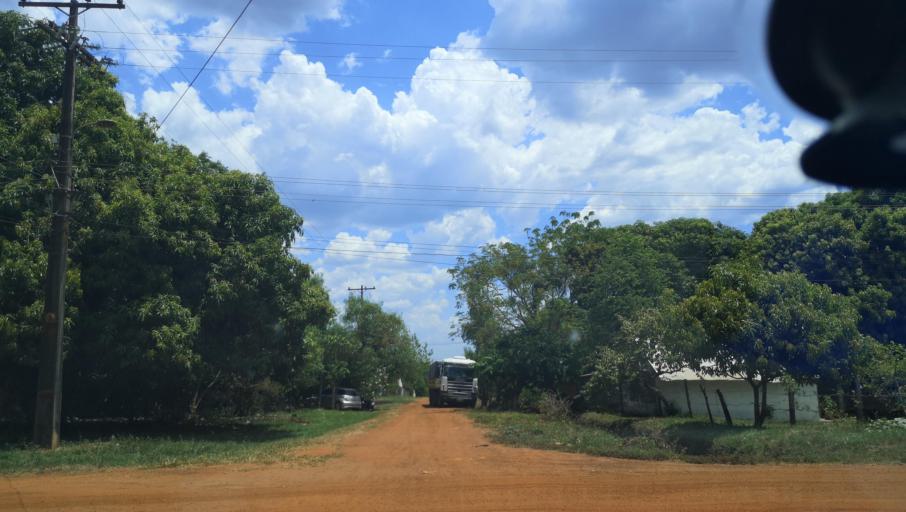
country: PY
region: Itapua
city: Carmen del Parana
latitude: -27.1699
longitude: -56.2406
